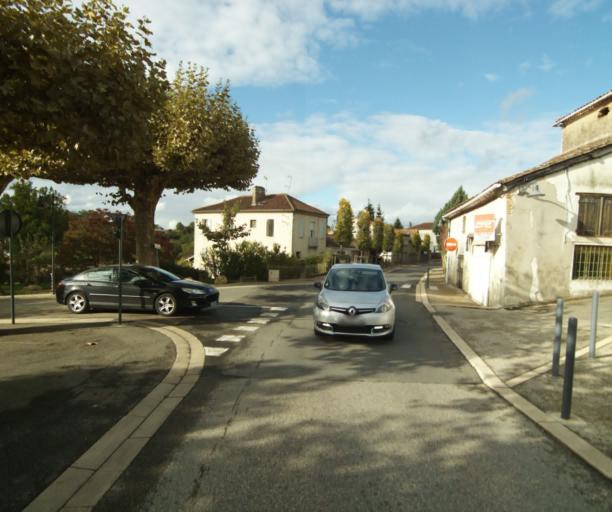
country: FR
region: Midi-Pyrenees
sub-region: Departement du Gers
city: Eauze
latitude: 43.8610
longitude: 0.0986
